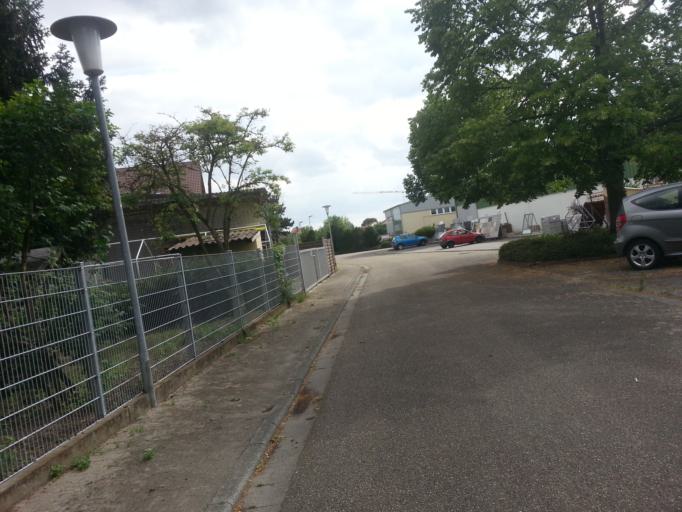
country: DE
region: Baden-Wuerttemberg
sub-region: Karlsruhe Region
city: Ladenburg
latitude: 49.4776
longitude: 8.6003
